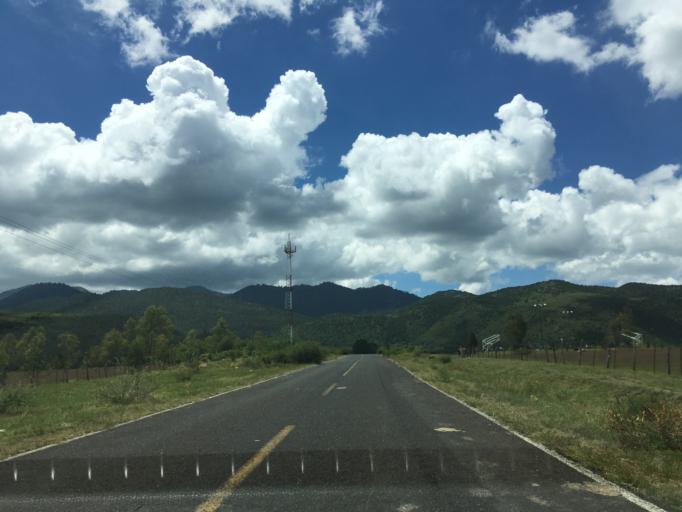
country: MX
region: Mexico
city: Huaniqueo de Morales
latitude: 19.7939
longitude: -101.4617
